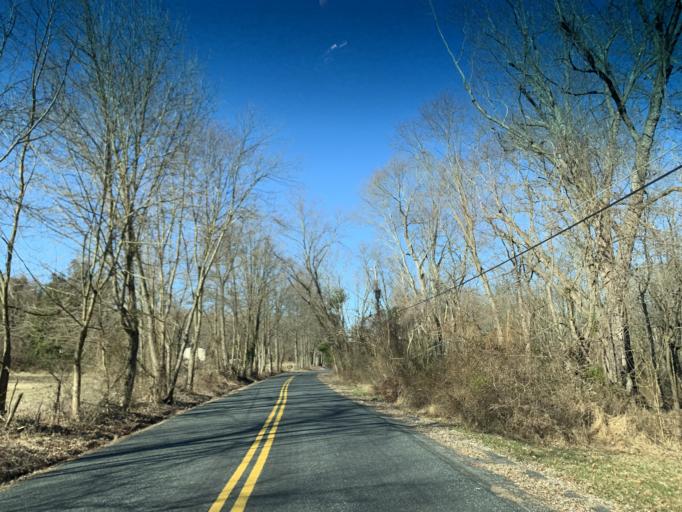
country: US
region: Maryland
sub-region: Harford County
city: South Bel Air
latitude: 39.6265
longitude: -76.2775
